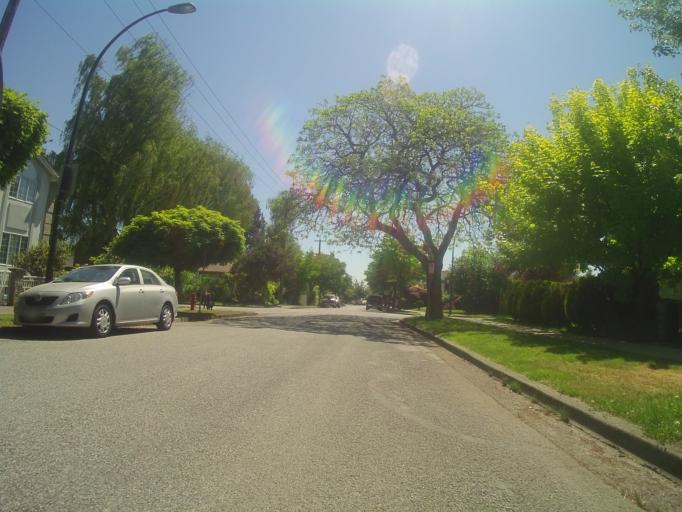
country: CA
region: British Columbia
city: Vancouver
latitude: 49.2288
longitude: -123.1059
